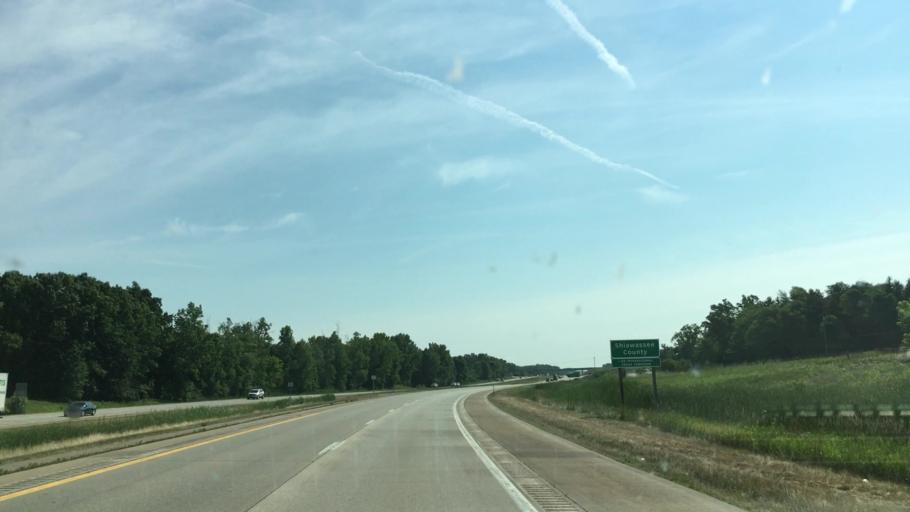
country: US
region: Michigan
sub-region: Ingham County
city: Haslett
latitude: 42.7958
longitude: -84.3641
